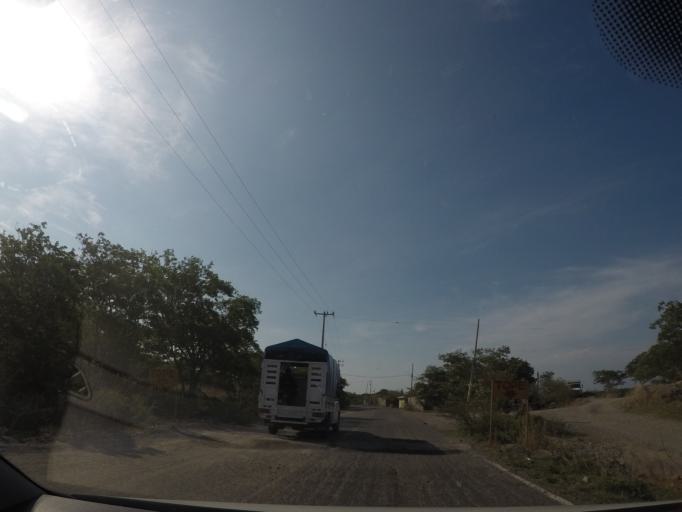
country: MX
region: Oaxaca
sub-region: Salina Cruz
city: Salina Cruz
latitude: 16.2333
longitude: -95.1505
